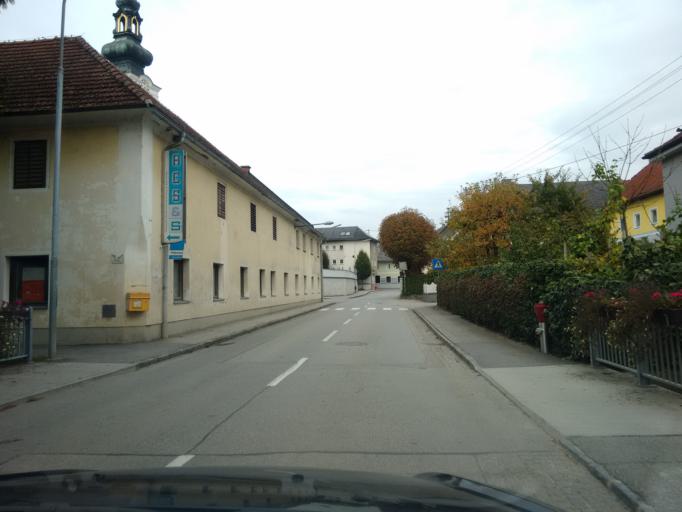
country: AT
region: Upper Austria
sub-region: Politischer Bezirk Grieskirchen
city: Bad Schallerbach
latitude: 48.1839
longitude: 13.8985
